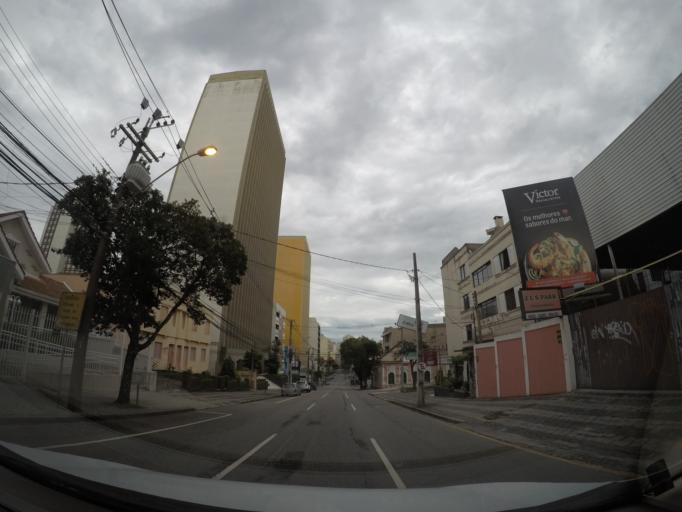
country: BR
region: Parana
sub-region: Curitiba
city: Curitiba
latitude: -25.4250
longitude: -49.2604
